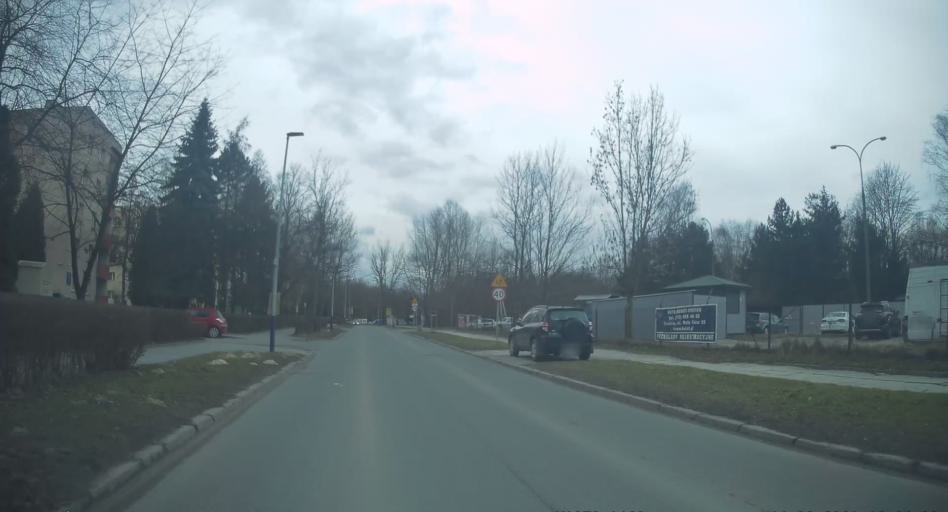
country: PL
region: Lesser Poland Voivodeship
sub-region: Powiat wielicki
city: Czarnochowice
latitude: 50.0142
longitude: 20.0164
